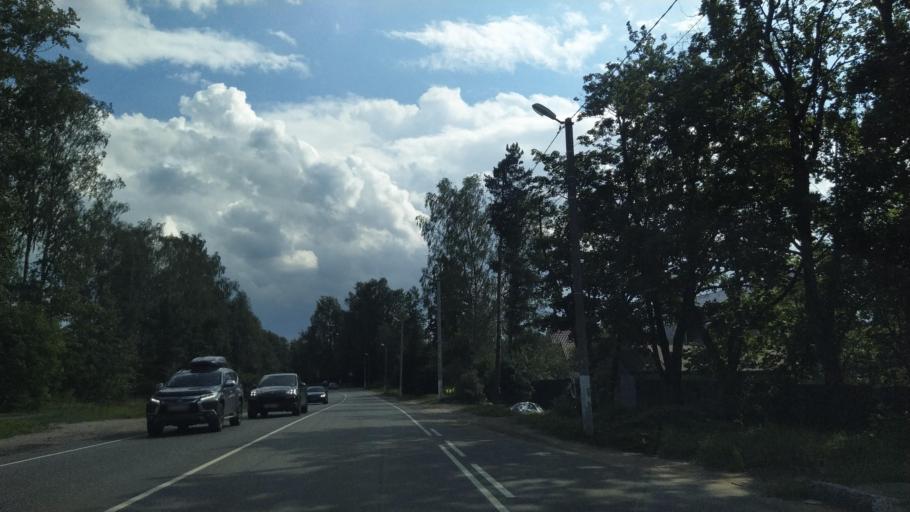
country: RU
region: Leningrad
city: Toksovo
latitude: 60.1481
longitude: 30.5231
